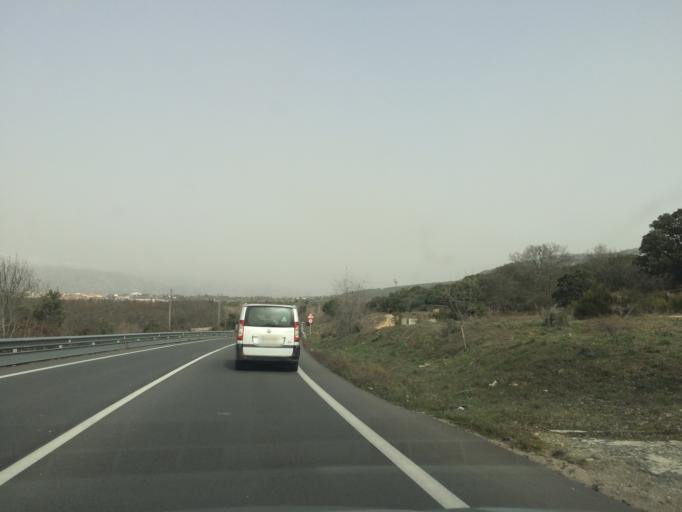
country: ES
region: Madrid
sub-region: Provincia de Madrid
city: Collado-Villalba
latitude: 40.6540
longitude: -3.9868
